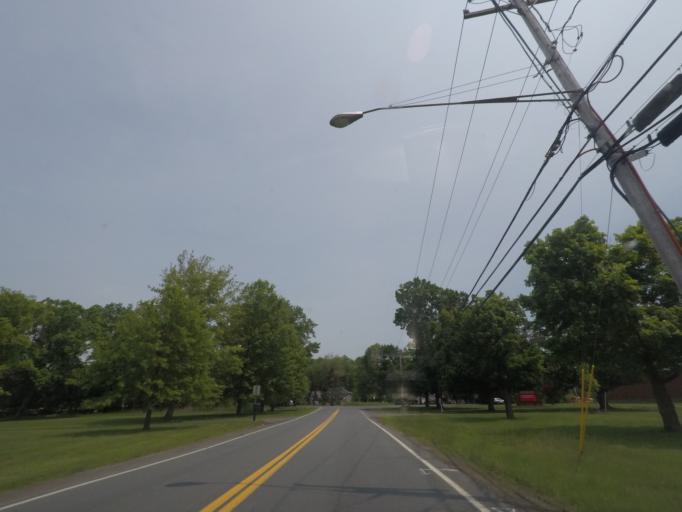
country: US
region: New York
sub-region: Rensselaer County
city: Castleton-on-Hudson
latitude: 42.5243
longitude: -73.7119
